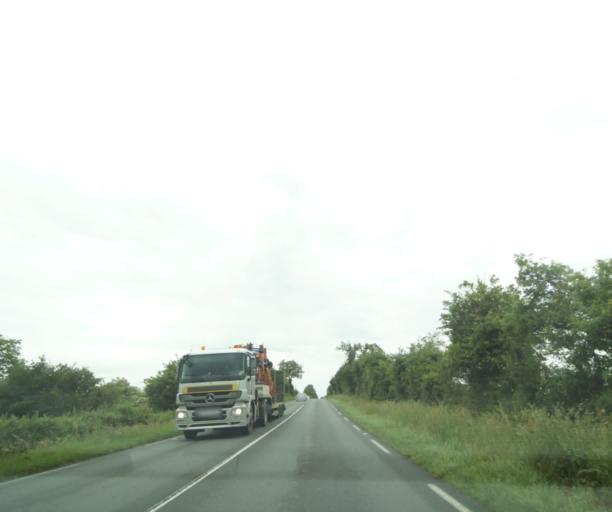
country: FR
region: Poitou-Charentes
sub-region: Departement des Deux-Sevres
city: Viennay
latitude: 46.7160
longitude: -0.2391
